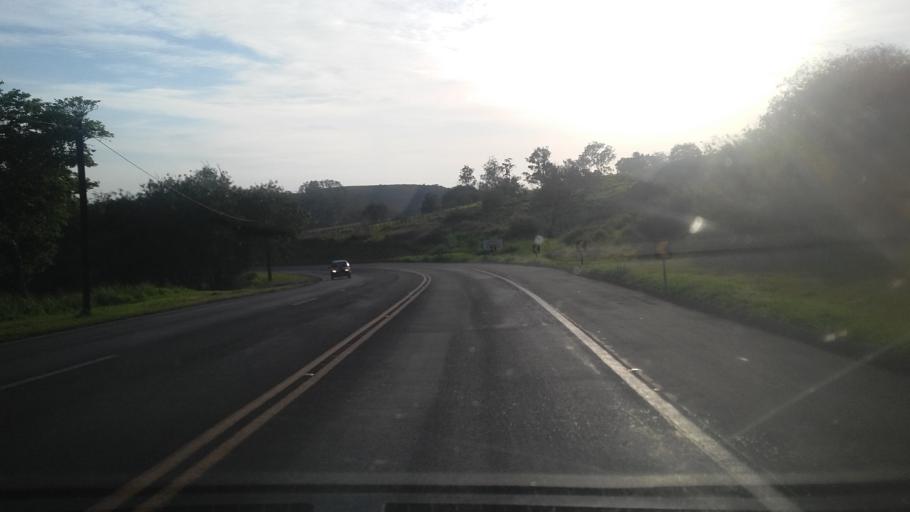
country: BR
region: Parana
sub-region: Bandeirantes
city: Bandeirantes
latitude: -23.1828
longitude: -50.6343
